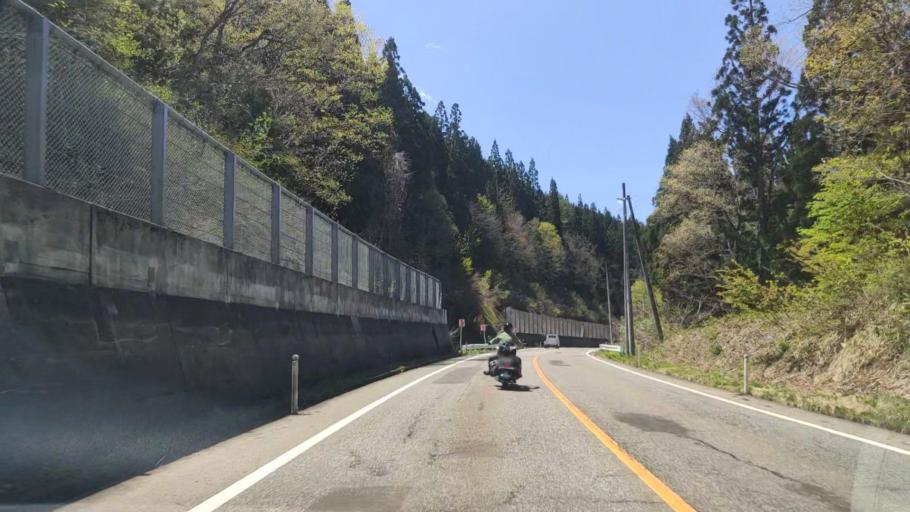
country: JP
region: Akita
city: Yuzawa
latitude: 39.0479
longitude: 140.4231
